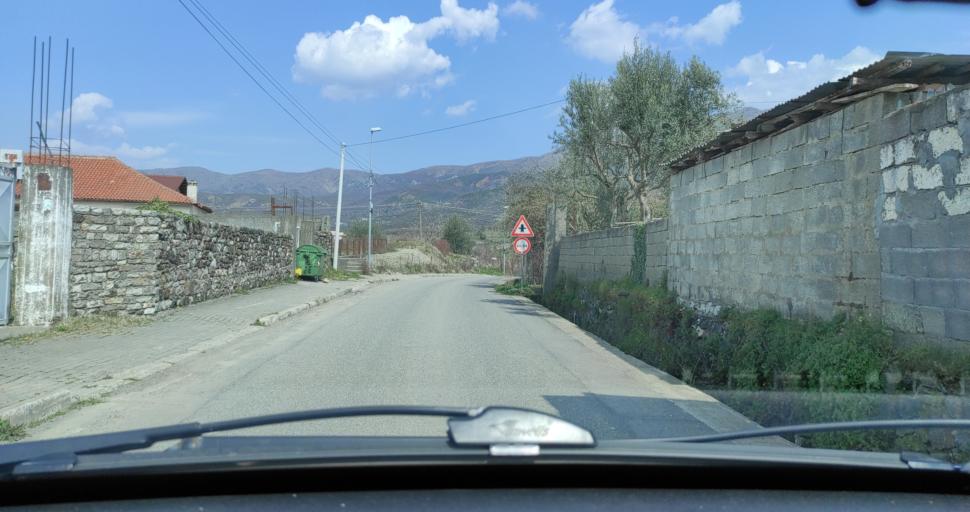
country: AL
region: Lezhe
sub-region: Rrethi i Lezhes
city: Kallmeti i Madh
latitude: 41.8585
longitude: 19.6970
